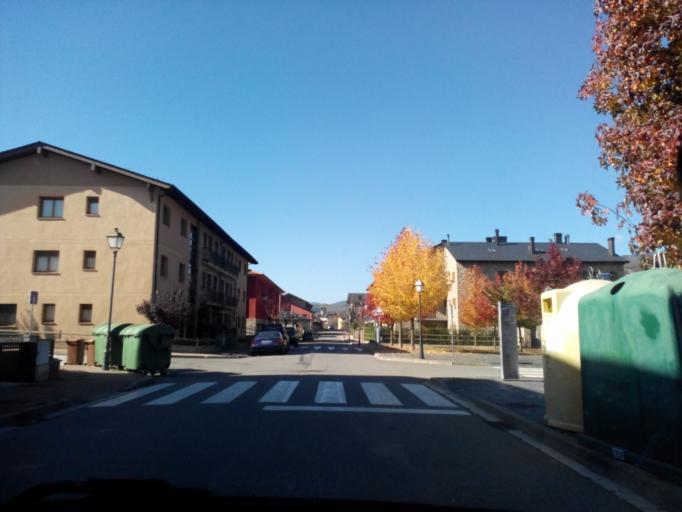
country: ES
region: Catalonia
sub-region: Provincia de Lleida
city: Bellver de Cerdanya
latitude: 42.3687
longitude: 1.7818
